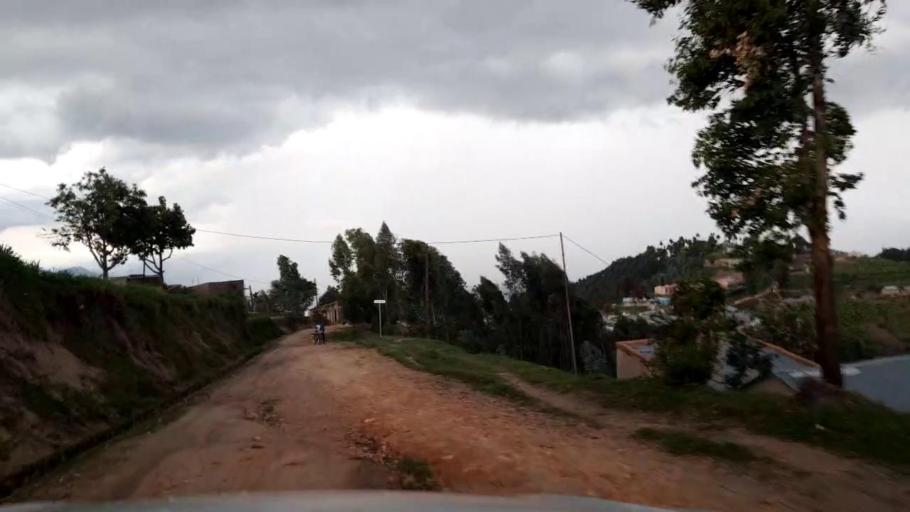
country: RW
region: Southern Province
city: Gitarama
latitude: -1.8720
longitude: 29.5888
